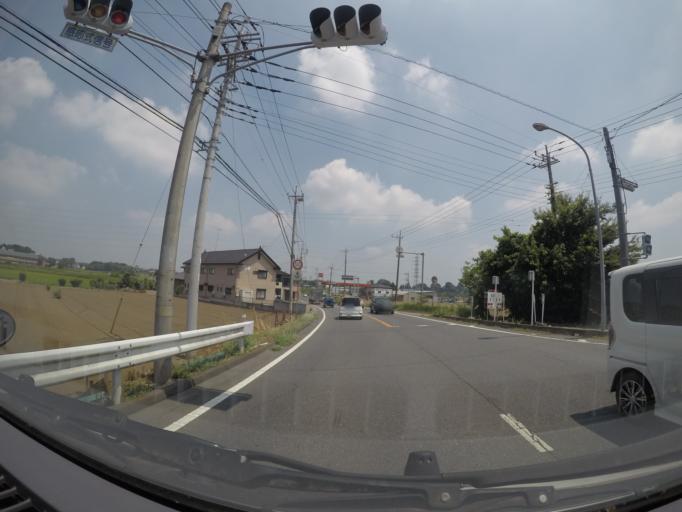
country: JP
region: Ibaraki
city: Sakai
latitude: 36.1998
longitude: 139.8298
